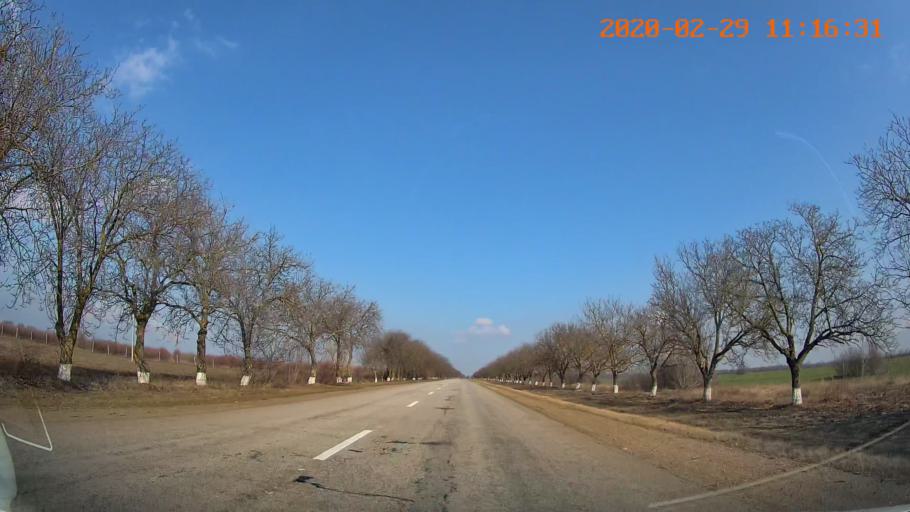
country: MD
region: Telenesti
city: Dubasari
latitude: 47.3099
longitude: 29.1680
